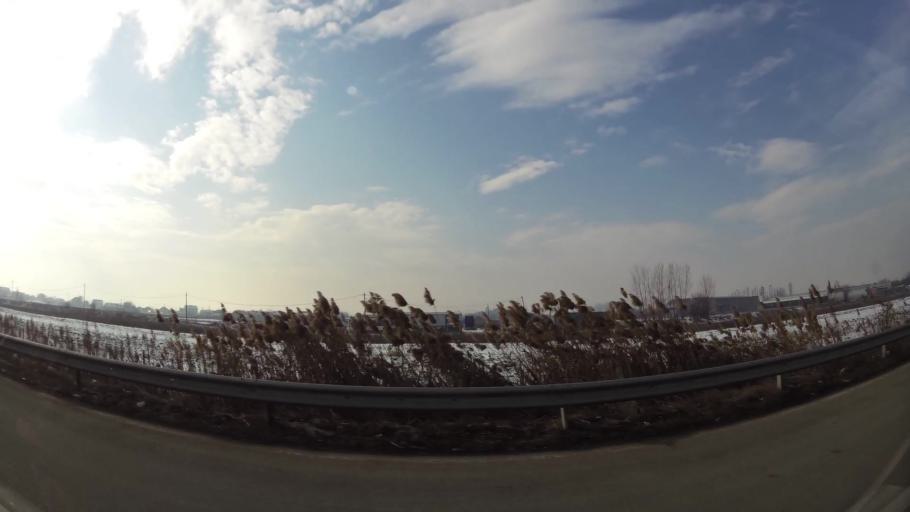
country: MK
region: Aracinovo
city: Arachinovo
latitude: 42.0154
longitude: 21.5342
